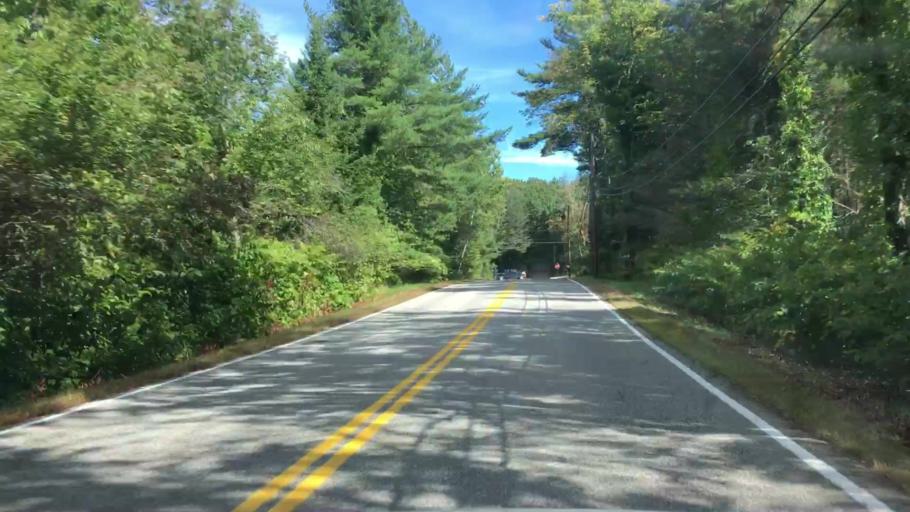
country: US
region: Maine
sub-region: Cumberland County
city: West Scarborough
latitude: 43.5815
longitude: -70.4587
